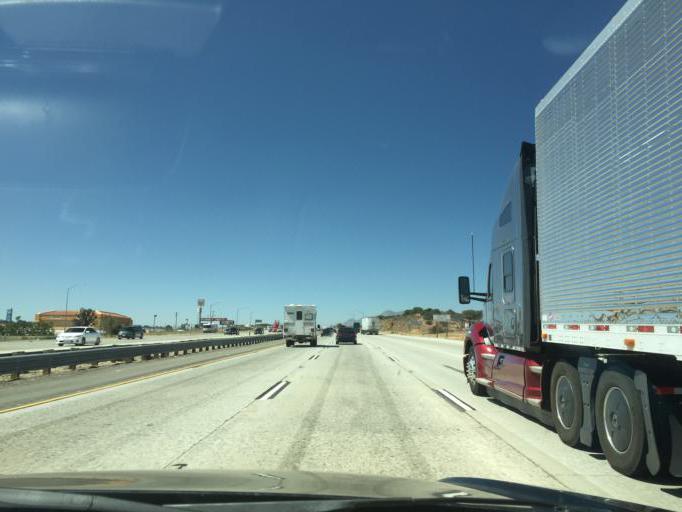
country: US
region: California
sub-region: San Bernardino County
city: Oak Hills
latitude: 34.3619
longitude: -117.4339
